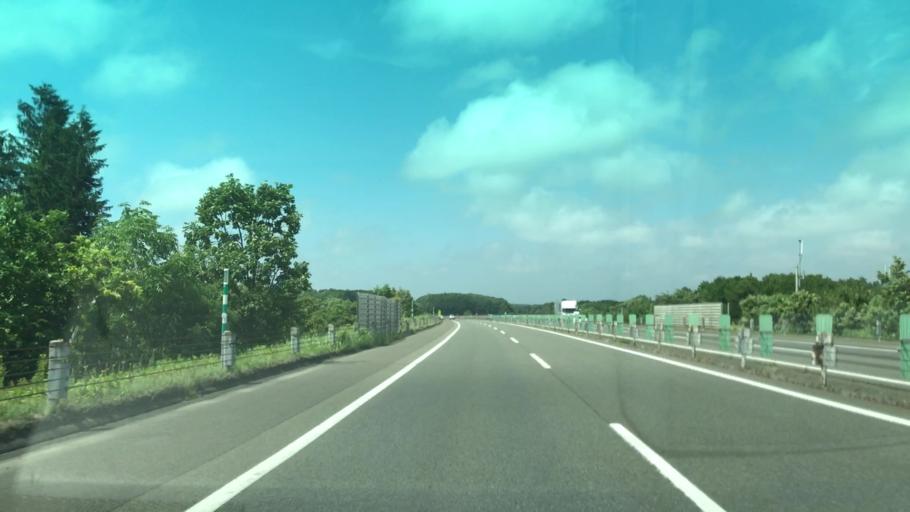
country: JP
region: Hokkaido
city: Kitahiroshima
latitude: 42.9115
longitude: 141.5495
